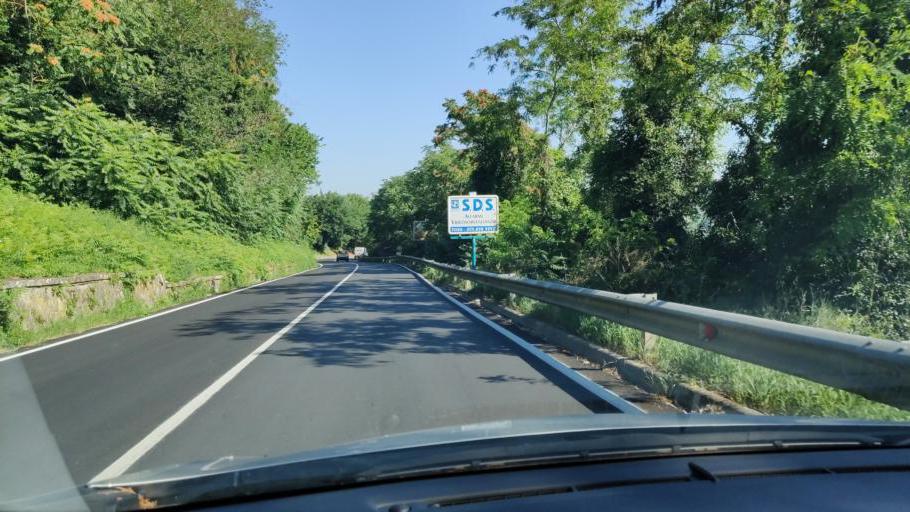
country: IT
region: Umbria
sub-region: Provincia di Perugia
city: Todi
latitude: 42.7810
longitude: 12.4193
